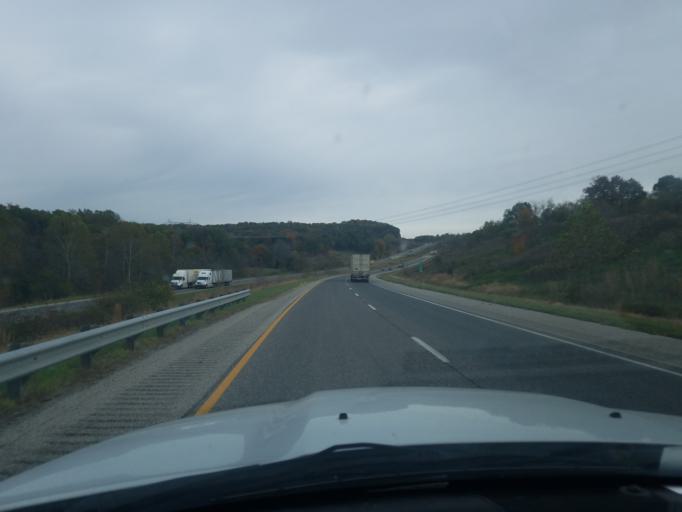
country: US
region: Indiana
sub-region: Dubois County
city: Ferdinand
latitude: 38.2152
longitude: -86.7415
